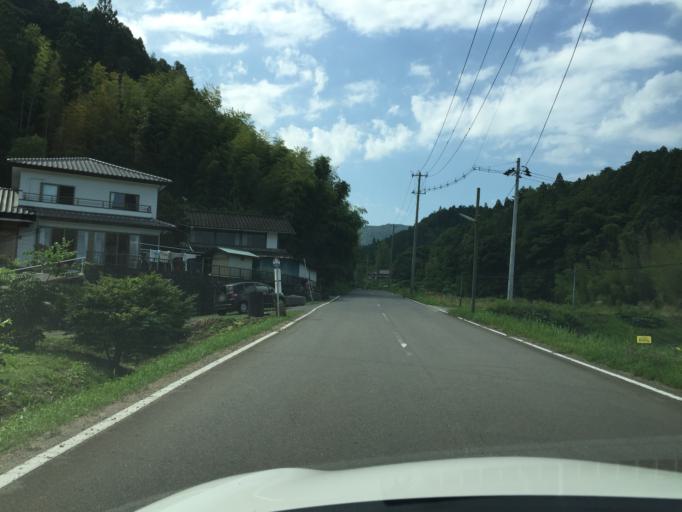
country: JP
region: Fukushima
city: Iwaki
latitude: 37.0540
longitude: 140.6939
